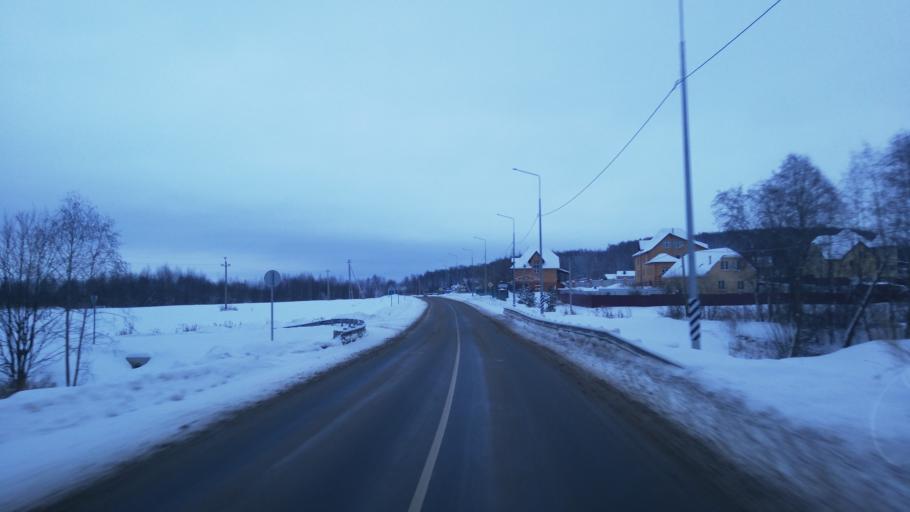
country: RU
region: Jaroslavl
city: Yaroslavl
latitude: 57.4977
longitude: 39.9261
